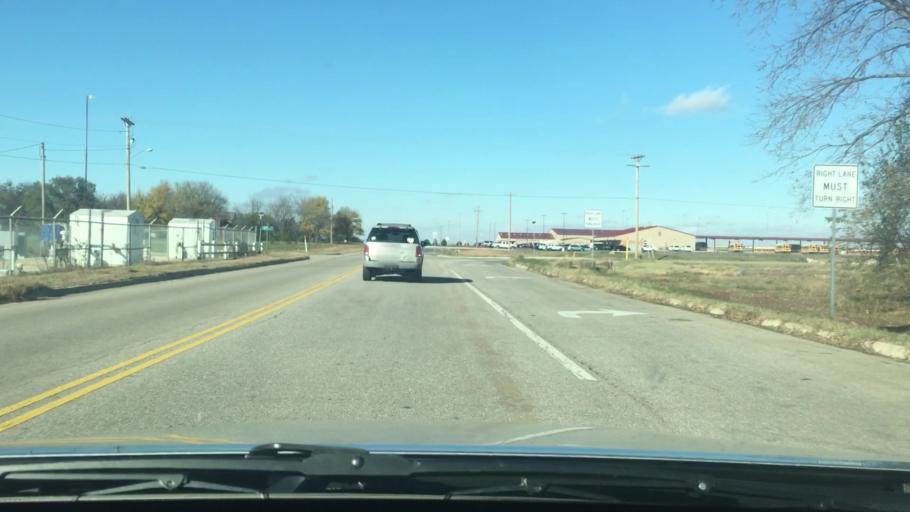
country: US
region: Kansas
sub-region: Sedgwick County
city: Maize
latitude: 37.7651
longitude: -97.4808
